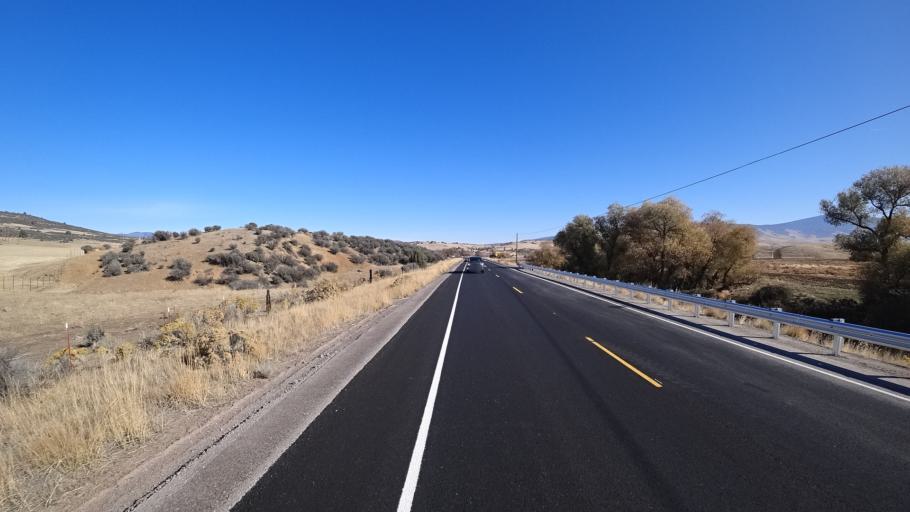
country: US
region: California
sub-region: Siskiyou County
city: Montague
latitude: 41.8410
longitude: -122.4784
